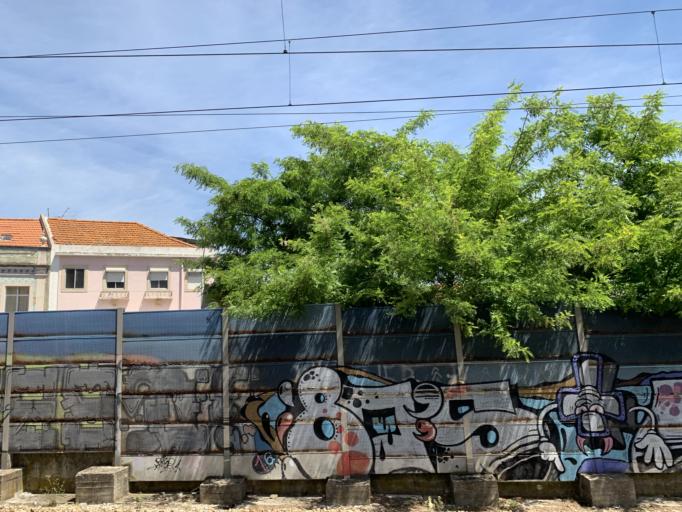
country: PT
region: Lisbon
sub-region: Amadora
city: Amadora
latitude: 38.7579
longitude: -9.2316
